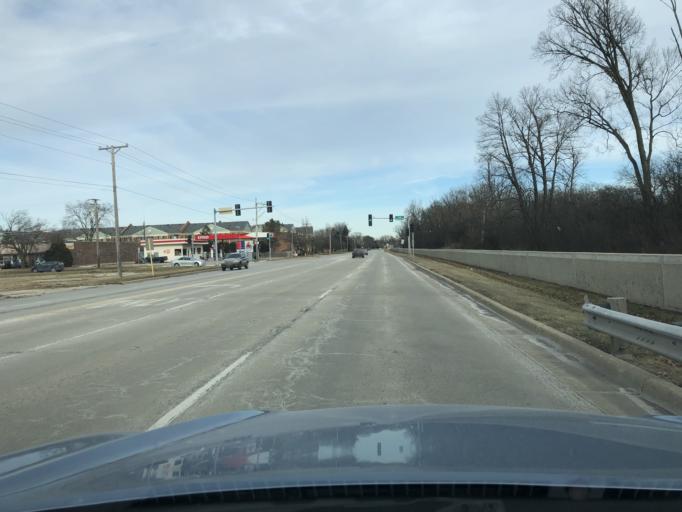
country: US
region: Illinois
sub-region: Cook County
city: Prospect Heights
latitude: 42.0942
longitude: -87.8909
